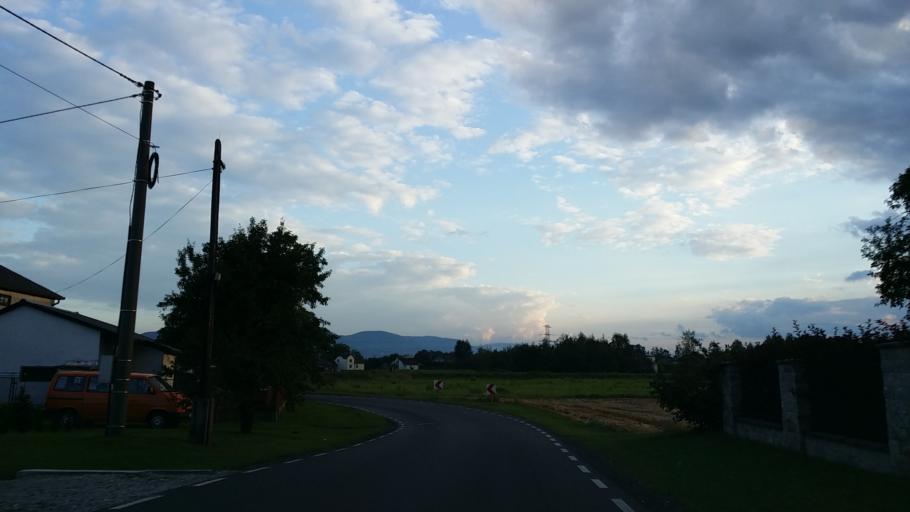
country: PL
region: Lesser Poland Voivodeship
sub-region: Powiat oswiecimski
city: Nowa Wies
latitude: 49.9116
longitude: 19.2296
